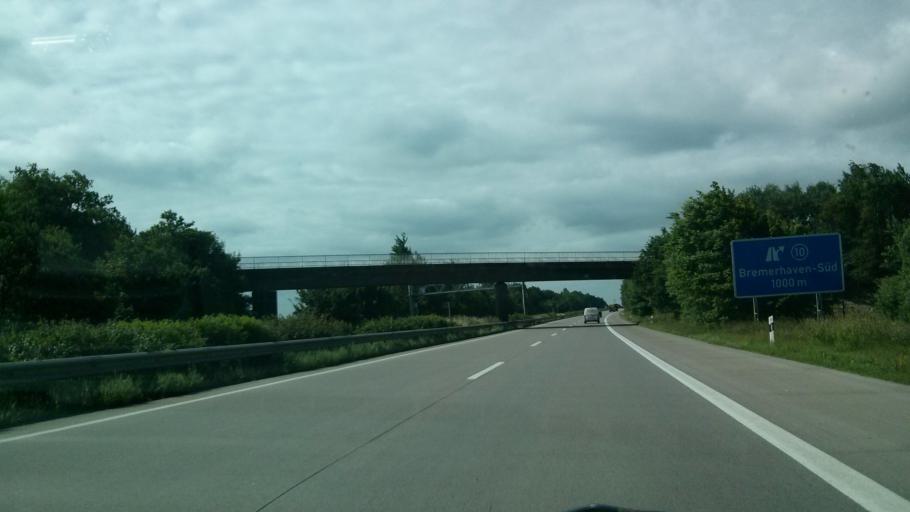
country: DE
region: Lower Saxony
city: Loxstedt
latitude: 53.4736
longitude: 8.6125
